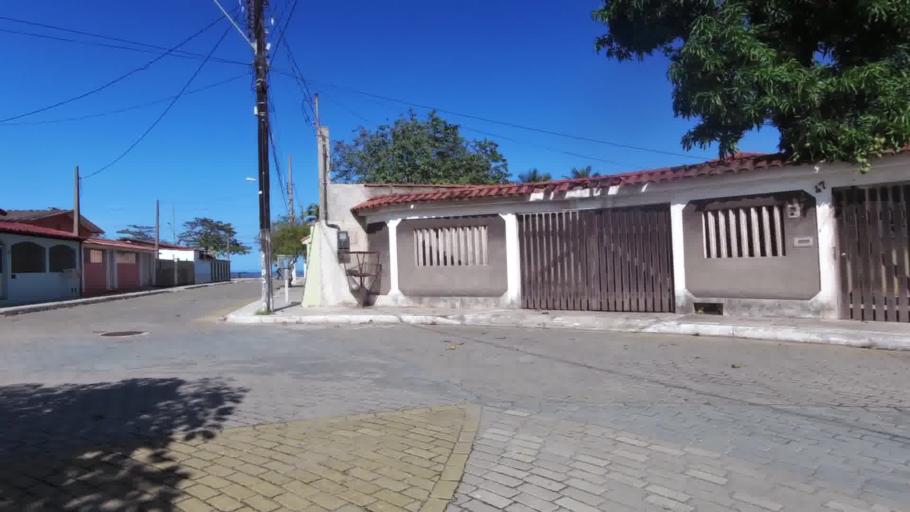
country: BR
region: Espirito Santo
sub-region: Piuma
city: Piuma
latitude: -20.8106
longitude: -40.6372
